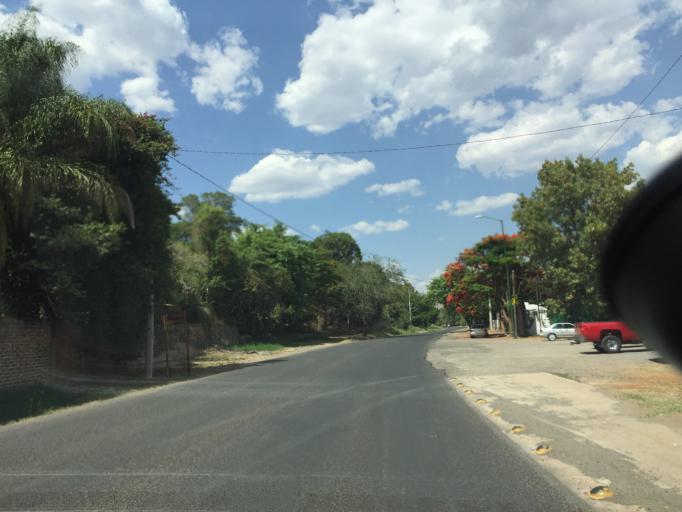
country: MX
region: Jalisco
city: Atotonilco el Alto
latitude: 20.5570
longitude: -102.4924
